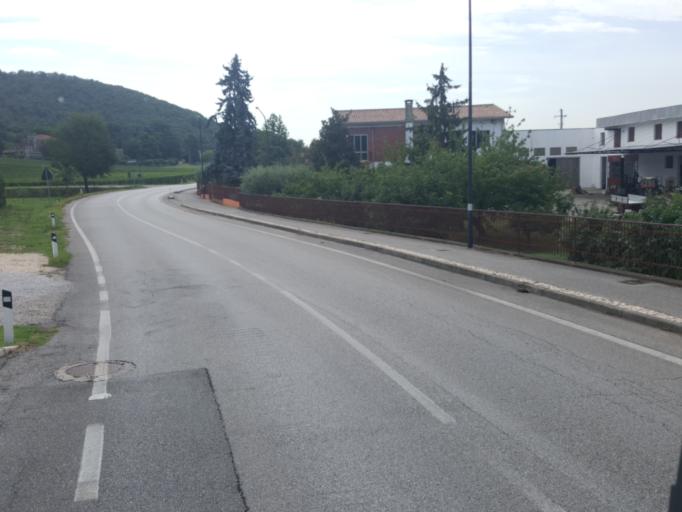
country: IT
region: Veneto
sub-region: Provincia di Padova
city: Galzignano
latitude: 45.2997
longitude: 11.7558
